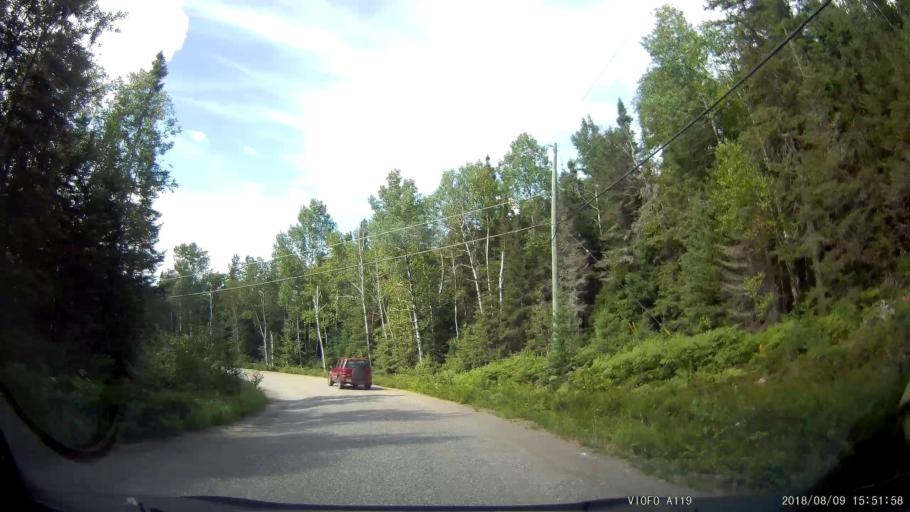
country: CA
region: Ontario
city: Rayside-Balfour
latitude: 46.5966
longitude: -81.5325
